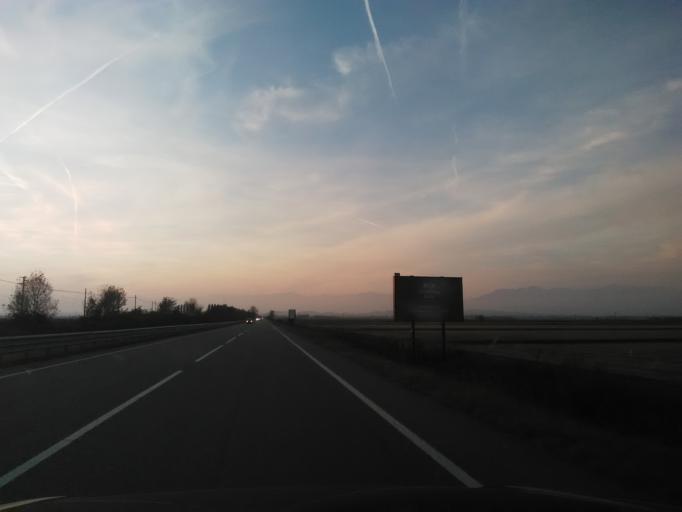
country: IT
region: Piedmont
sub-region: Provincia di Vercelli
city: San Germano Vercellese
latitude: 45.3542
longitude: 8.2246
